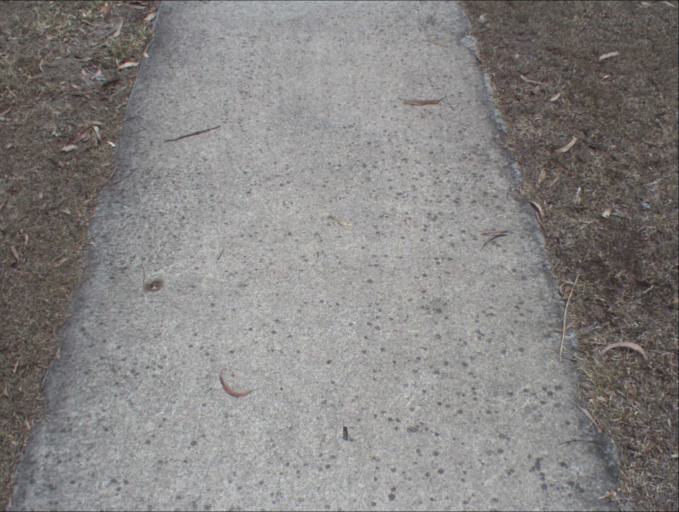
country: AU
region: Queensland
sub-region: Logan
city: Slacks Creek
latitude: -27.6588
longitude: 153.1970
